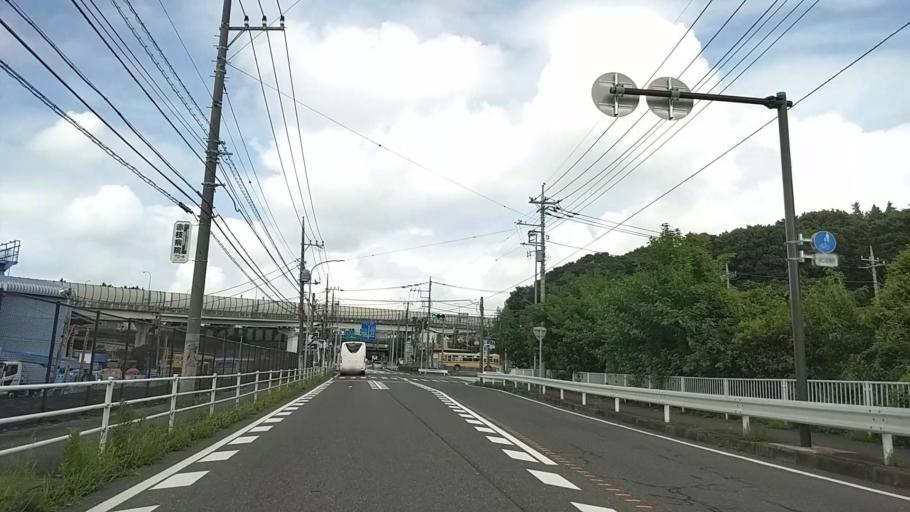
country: JP
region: Kanagawa
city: Minami-rinkan
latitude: 35.4971
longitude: 139.4971
